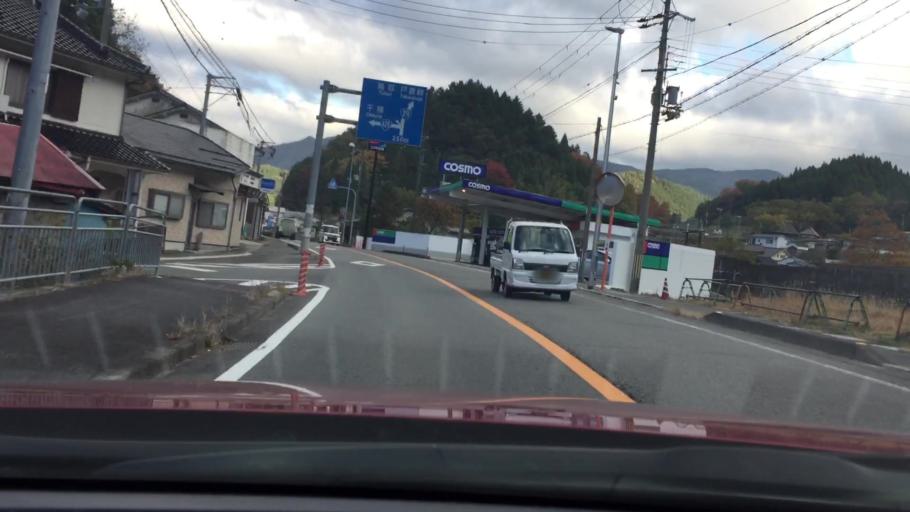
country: JP
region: Hyogo
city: Yamazakicho-nakabirose
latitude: 35.1571
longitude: 134.5457
